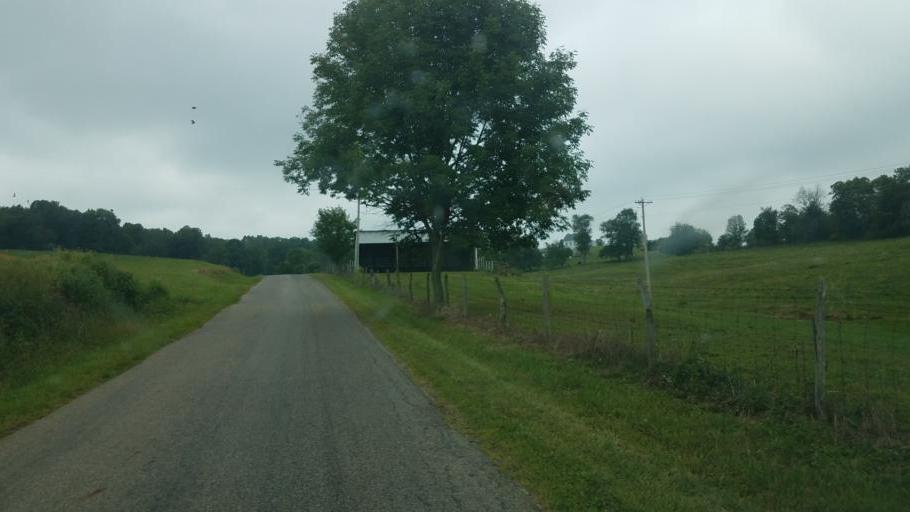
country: US
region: Ohio
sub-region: Licking County
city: Utica
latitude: 40.2443
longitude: -82.3770
